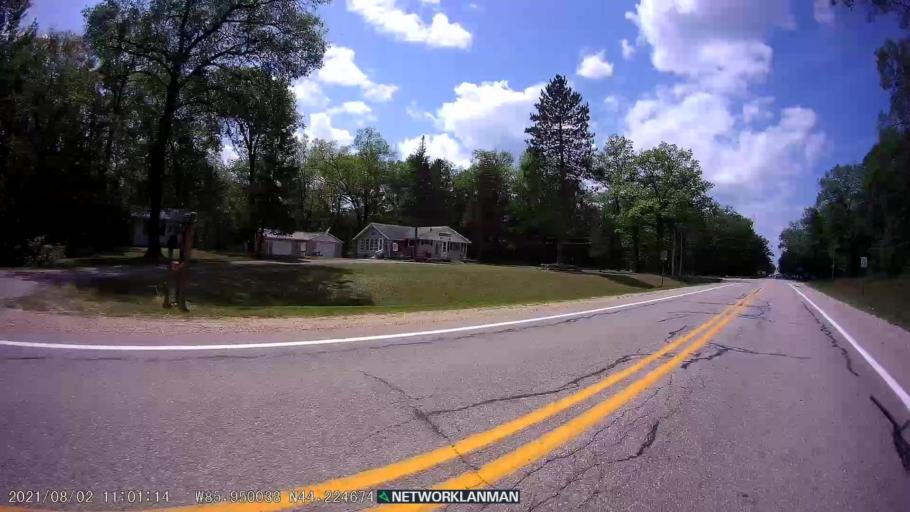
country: US
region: Michigan
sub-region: Lake County
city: Baldwin
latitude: 44.2245
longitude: -85.9509
